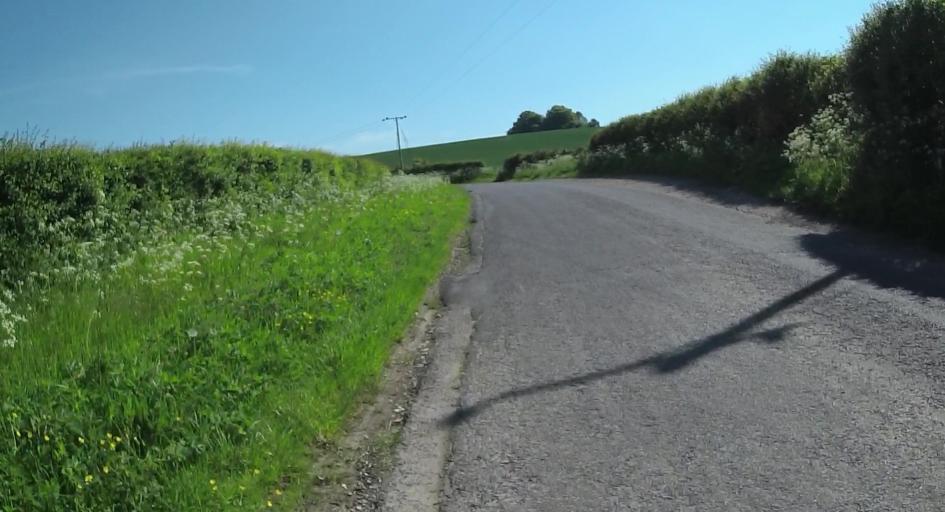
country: GB
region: England
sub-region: Hampshire
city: Kings Worthy
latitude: 51.0725
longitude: -1.2703
